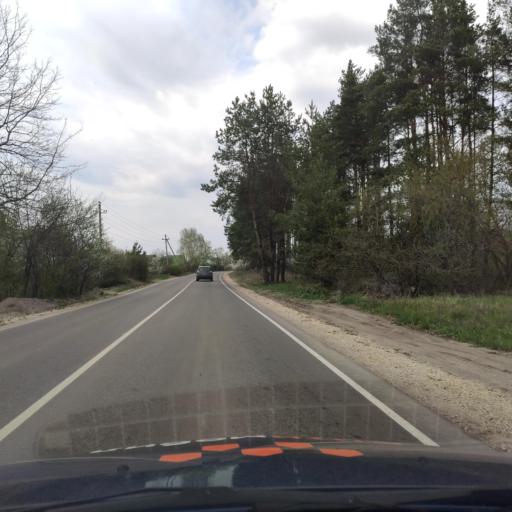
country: RU
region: Voronezj
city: Podgornoye
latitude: 51.8332
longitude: 39.1439
